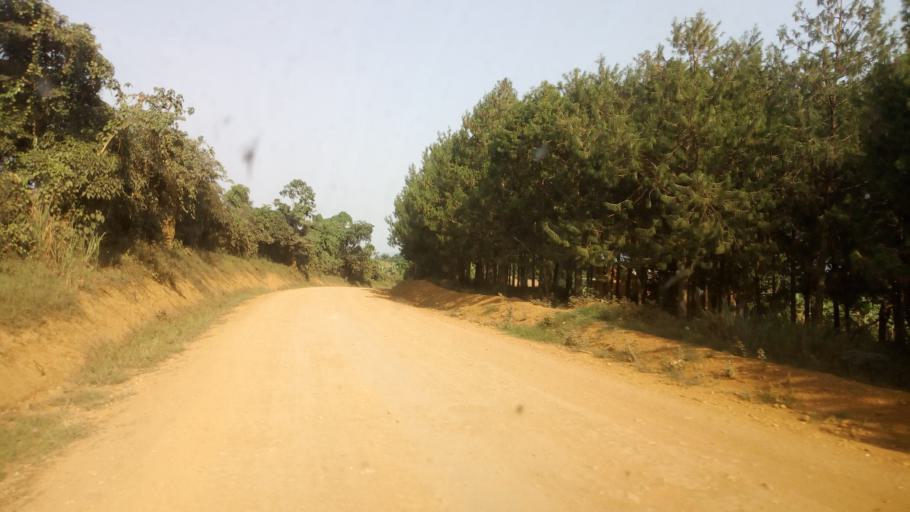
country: UG
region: Western Region
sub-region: Kanungu District
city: Ntungamo
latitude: -0.8278
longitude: 29.7032
